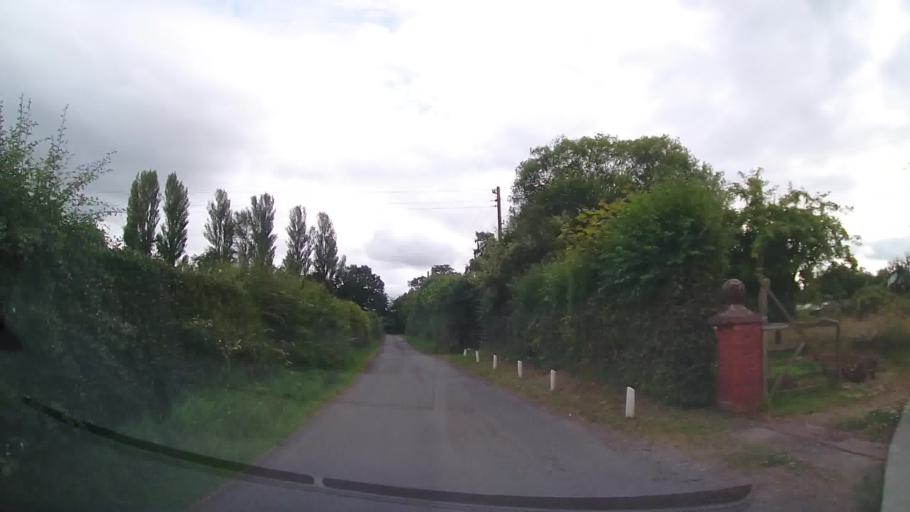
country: GB
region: England
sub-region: Shropshire
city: Prees
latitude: 52.9107
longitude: -2.7006
